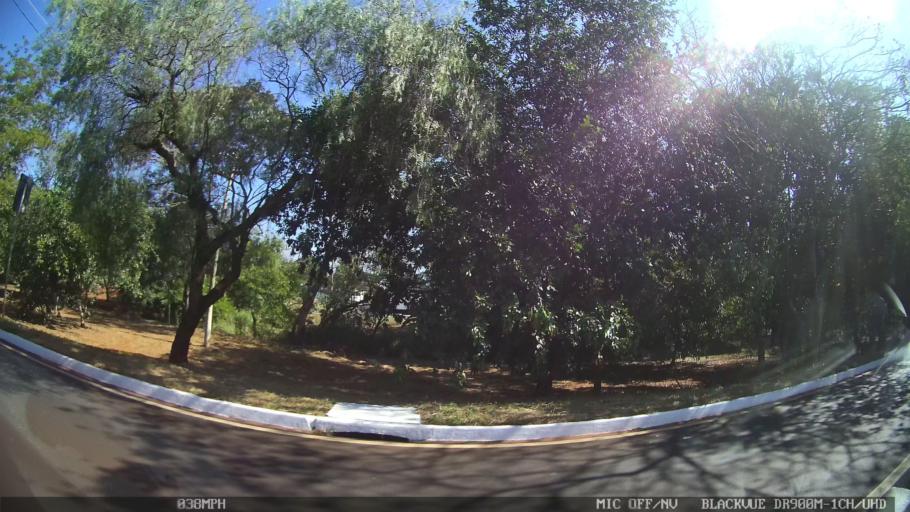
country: BR
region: Sao Paulo
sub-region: Ribeirao Preto
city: Ribeirao Preto
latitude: -21.2302
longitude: -47.7661
